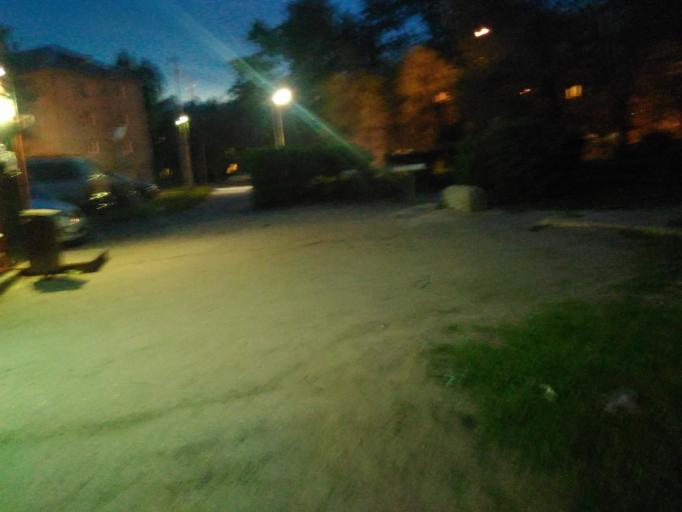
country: RU
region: Ulyanovsk
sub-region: Ulyanovskiy Rayon
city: Ulyanovsk
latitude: 54.2773
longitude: 48.3442
